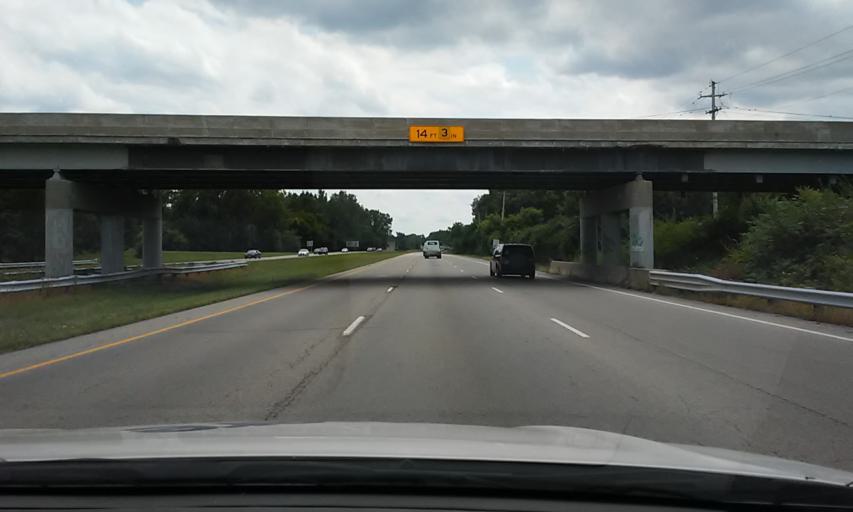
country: US
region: Ohio
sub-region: Greene County
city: Wright-Patterson AFB
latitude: 39.8440
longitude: -84.0592
